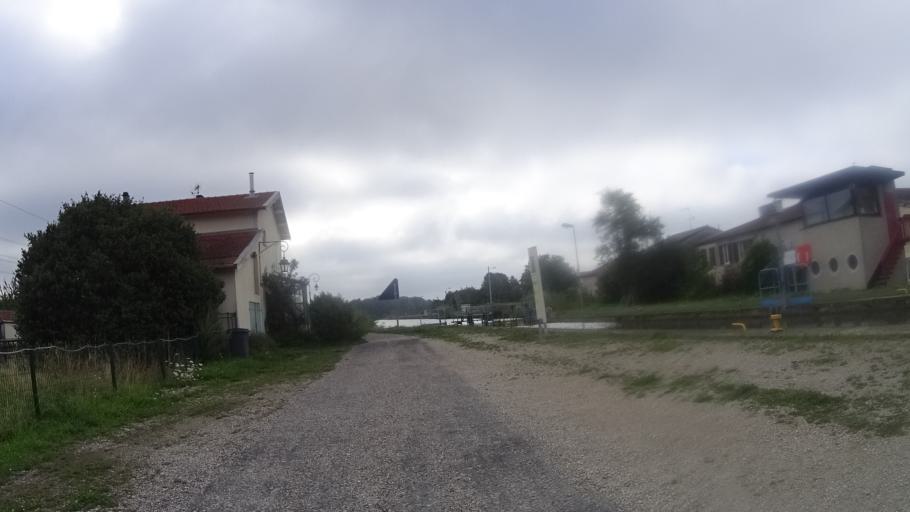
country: FR
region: Lorraine
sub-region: Departement de la Meuse
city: Fains-Veel
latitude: 48.7929
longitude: 5.1262
